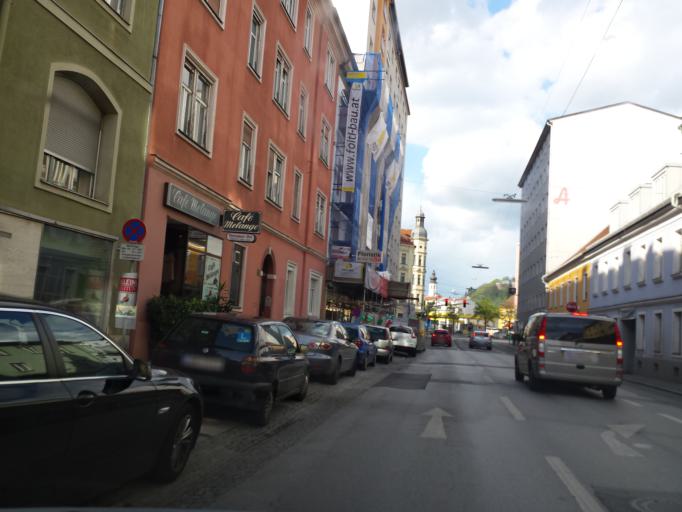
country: AT
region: Styria
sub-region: Graz Stadt
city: Graz
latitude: 47.0656
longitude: 15.4261
